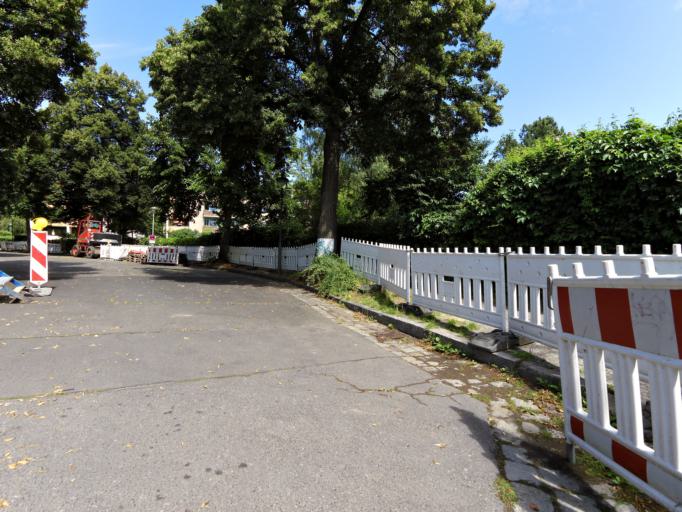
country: DE
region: Berlin
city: Lankwitz
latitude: 52.4448
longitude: 13.3464
